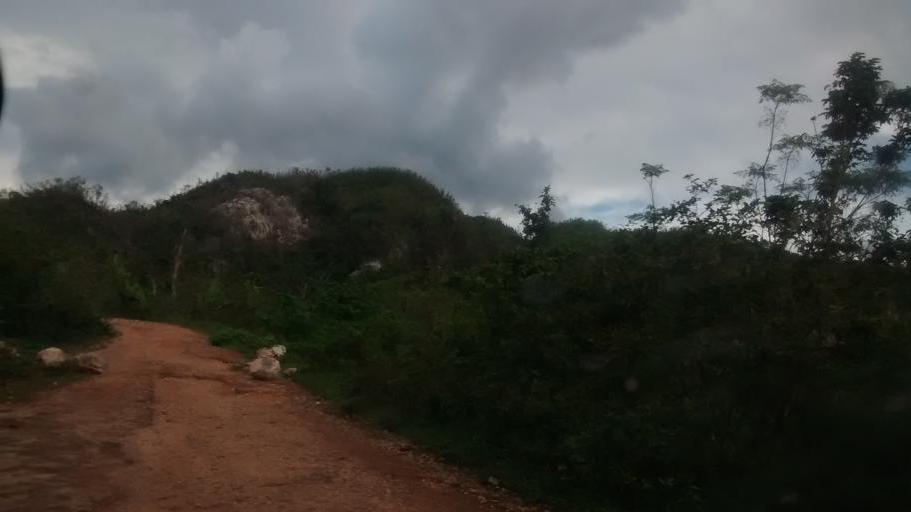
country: HT
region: Grandans
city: Corail
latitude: 18.5173
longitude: -73.7865
